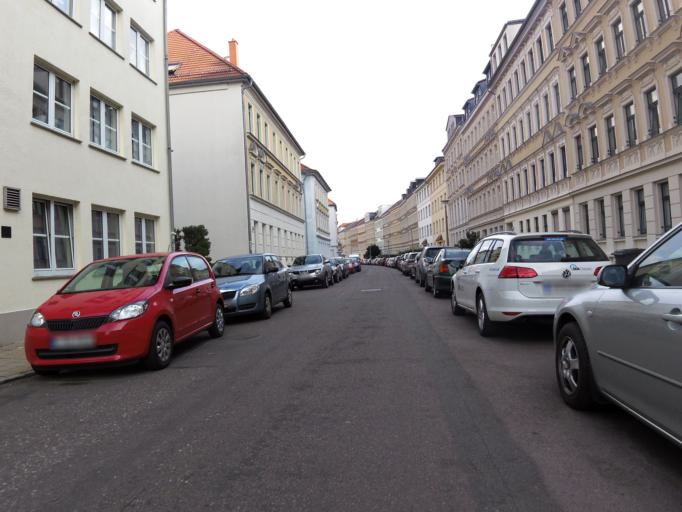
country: DE
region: Saxony
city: Leipzig
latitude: 51.3143
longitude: 12.3217
